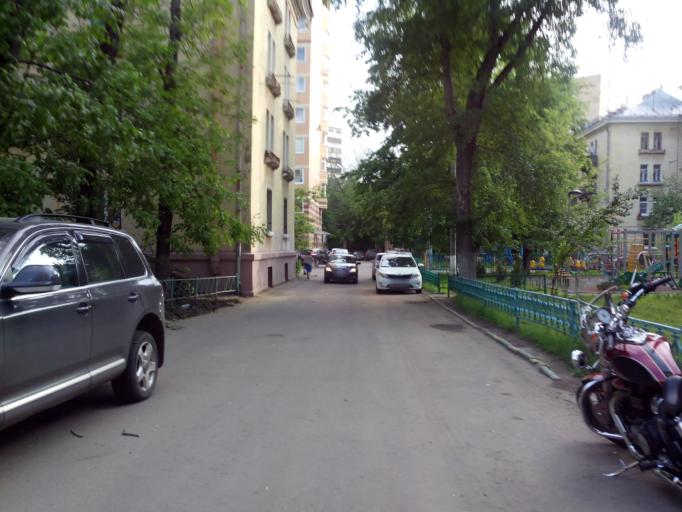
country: RU
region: Moscow
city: Lefortovo
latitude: 55.7739
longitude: 37.7065
